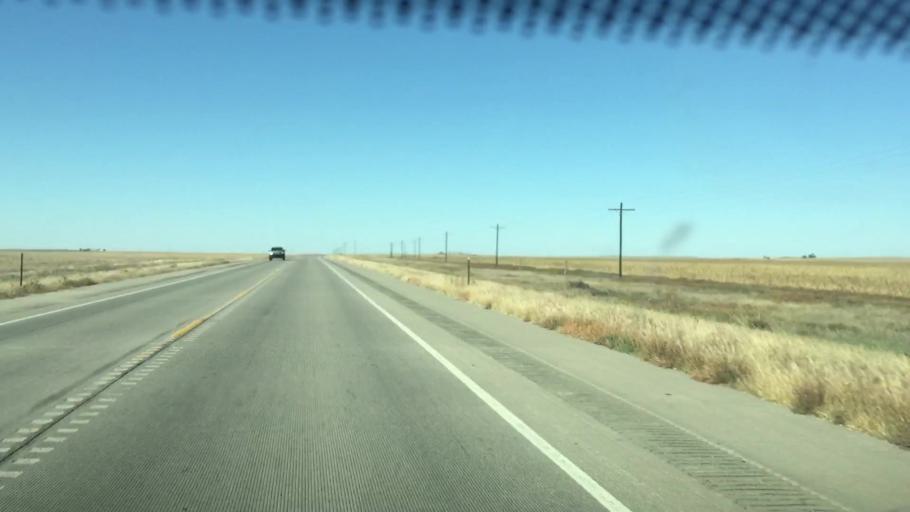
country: US
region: Colorado
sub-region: Kiowa County
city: Eads
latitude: 38.6731
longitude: -102.7859
